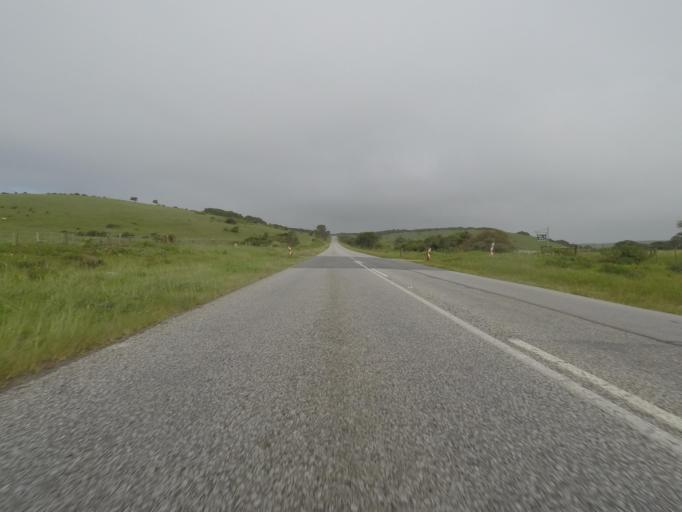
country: ZA
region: Eastern Cape
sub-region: Cacadu District Municipality
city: Port Alfred
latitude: -33.6059
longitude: 26.8335
